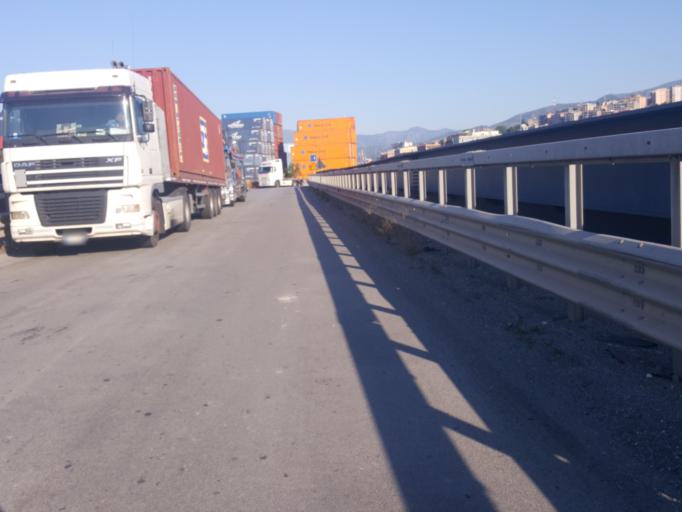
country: IT
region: Liguria
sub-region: Provincia di Genova
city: San Teodoro
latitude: 44.4113
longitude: 8.8777
